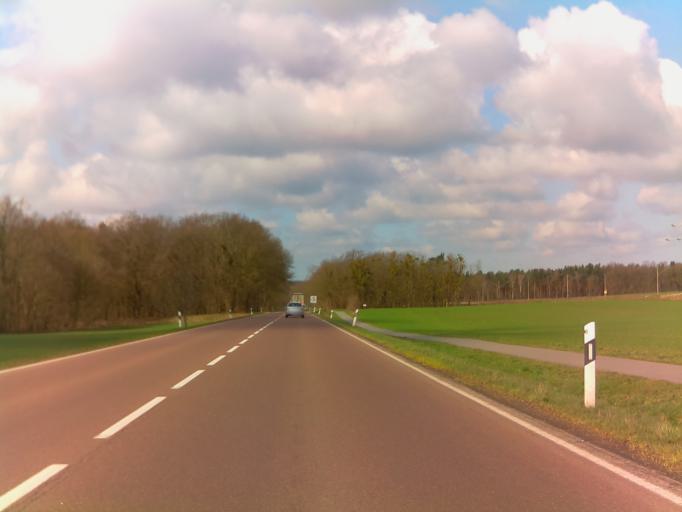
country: DE
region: Saxony-Anhalt
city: Klieken
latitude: 51.8900
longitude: 12.3963
